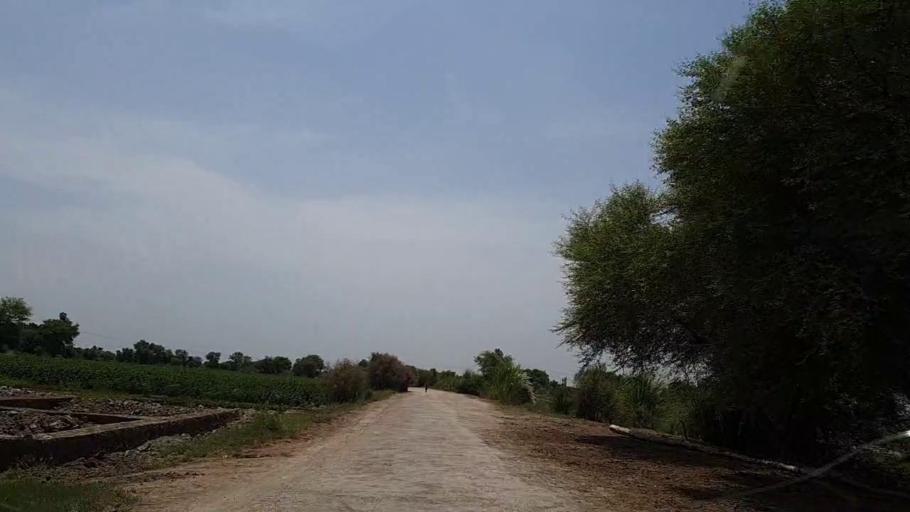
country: PK
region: Sindh
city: Khanpur
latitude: 27.8417
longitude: 69.4847
